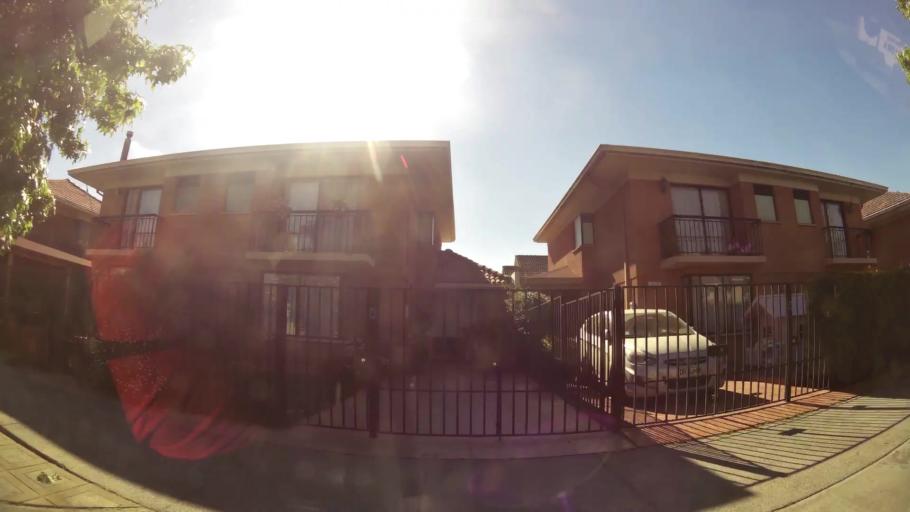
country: CL
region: Santiago Metropolitan
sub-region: Provincia de Maipo
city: San Bernardo
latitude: -33.5622
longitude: -70.7815
